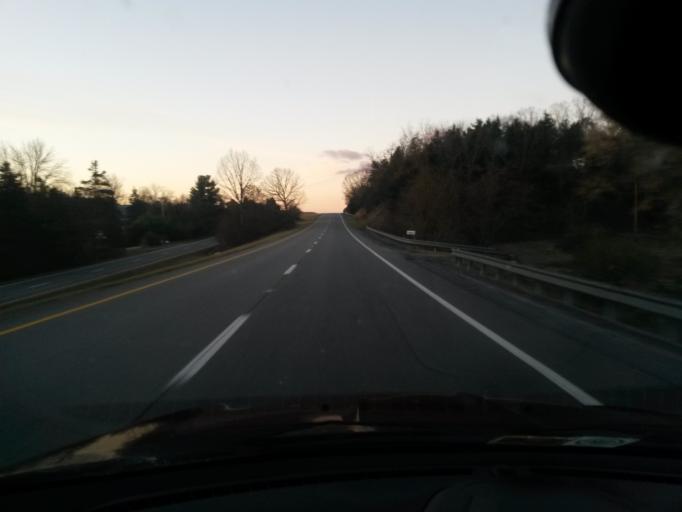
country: US
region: Virginia
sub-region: Botetourt County
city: Fincastle
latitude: 37.5342
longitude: -79.8685
